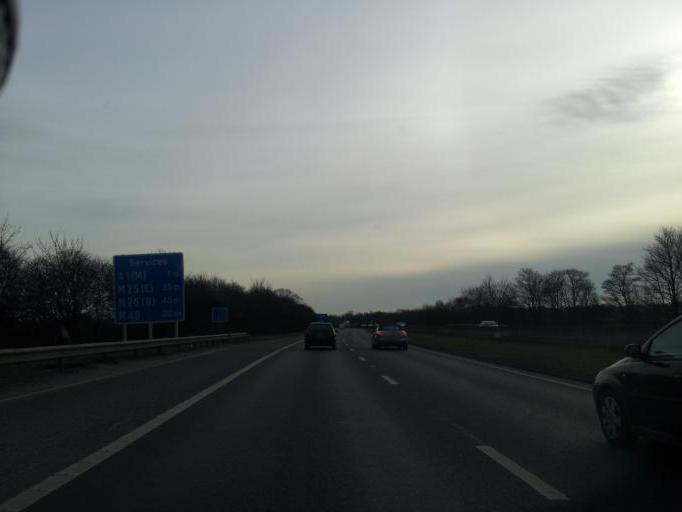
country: GB
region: England
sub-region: Hertfordshire
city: Potters Bar
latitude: 51.7048
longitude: -0.2206
